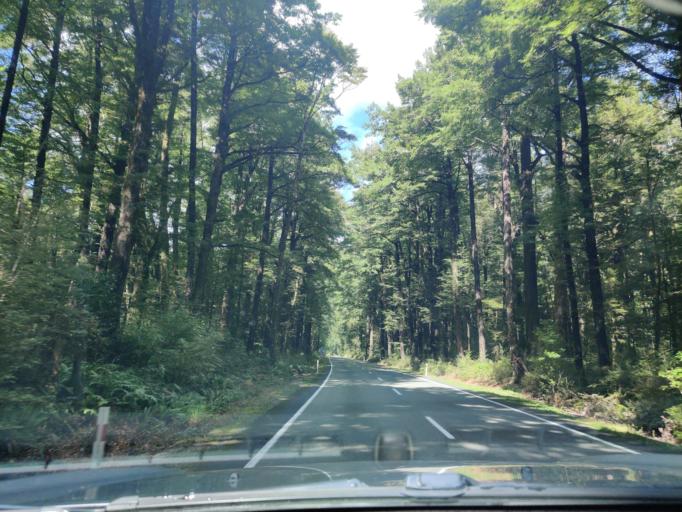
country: NZ
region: West Coast
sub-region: Buller District
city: Westport
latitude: -42.3760
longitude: 172.2730
